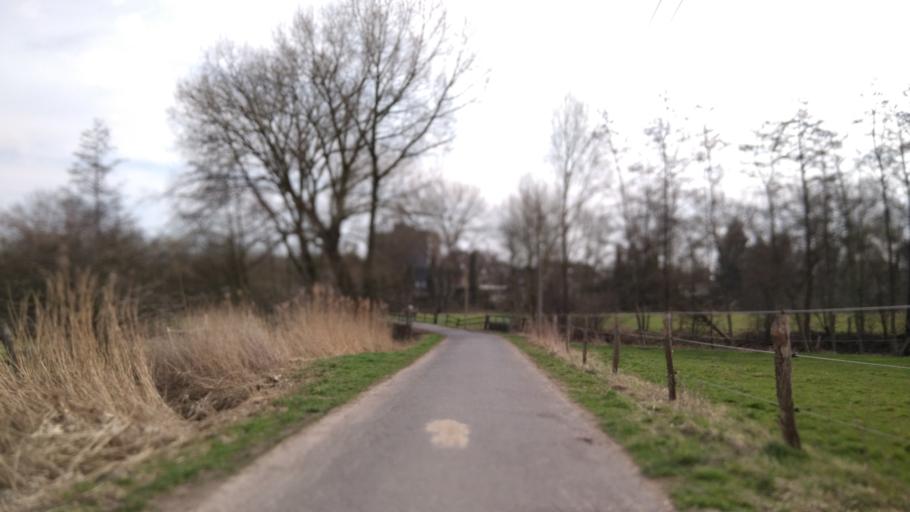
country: DE
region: North Rhine-Westphalia
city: Marl
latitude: 51.6110
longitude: 7.0897
